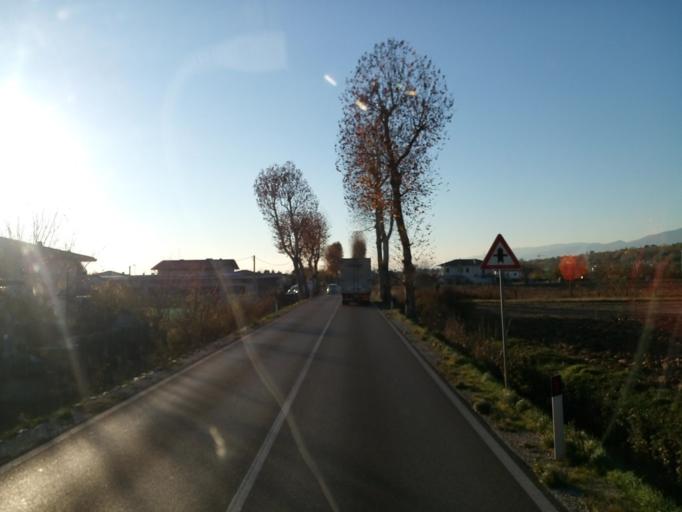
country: IT
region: Veneto
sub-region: Provincia di Treviso
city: Asolo
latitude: 45.7929
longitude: 11.9416
